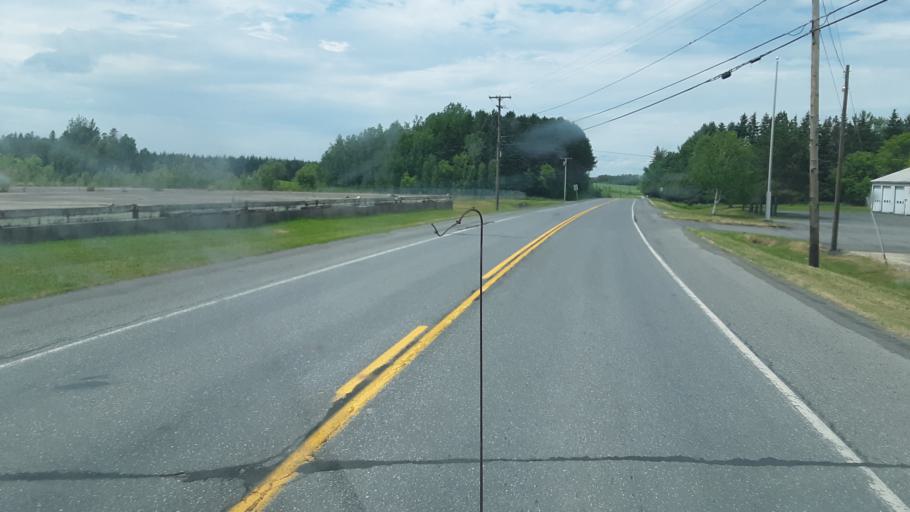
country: US
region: Maine
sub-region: Aroostook County
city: Fort Fairfield
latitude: 46.7778
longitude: -67.8448
